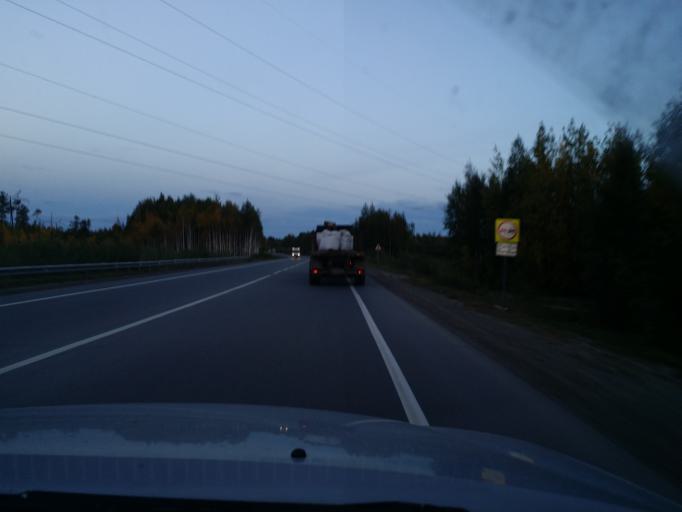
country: RU
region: Khanty-Mansiyskiy Avtonomnyy Okrug
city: Nizhnevartovsk
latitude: 61.0271
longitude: 76.3652
